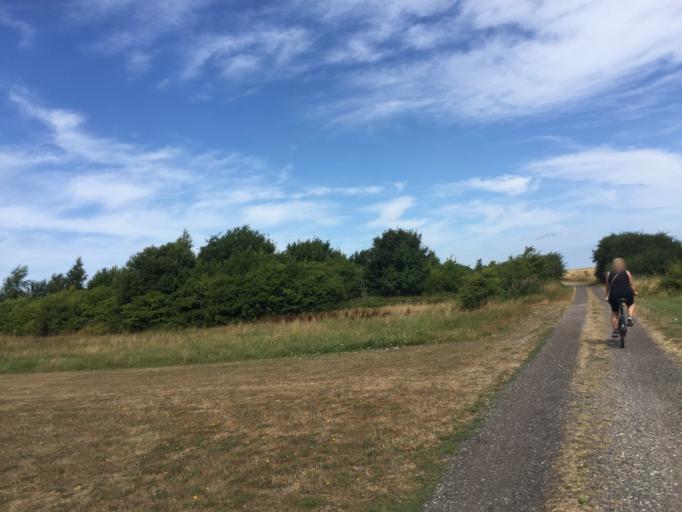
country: DK
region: Central Jutland
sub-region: Samso Kommune
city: Tranebjerg
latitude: 55.9571
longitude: 10.4117
